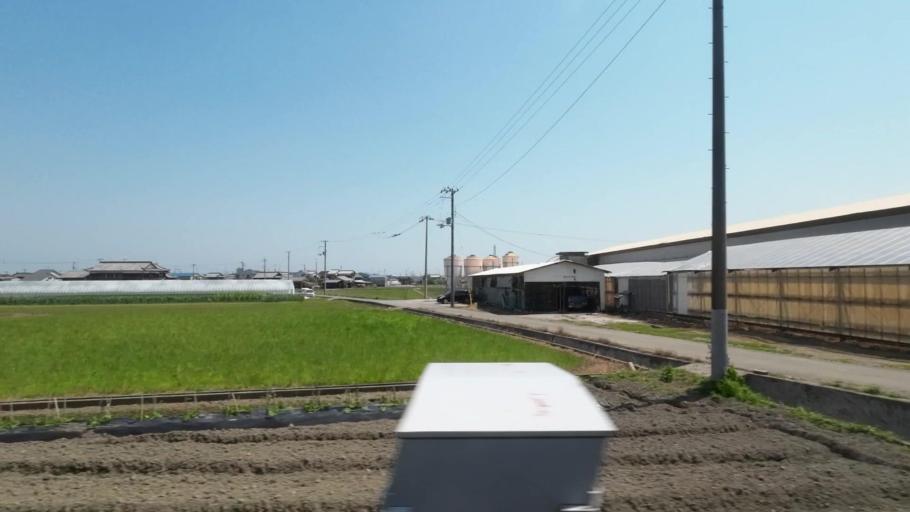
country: JP
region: Ehime
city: Saijo
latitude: 33.9225
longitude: 133.0919
